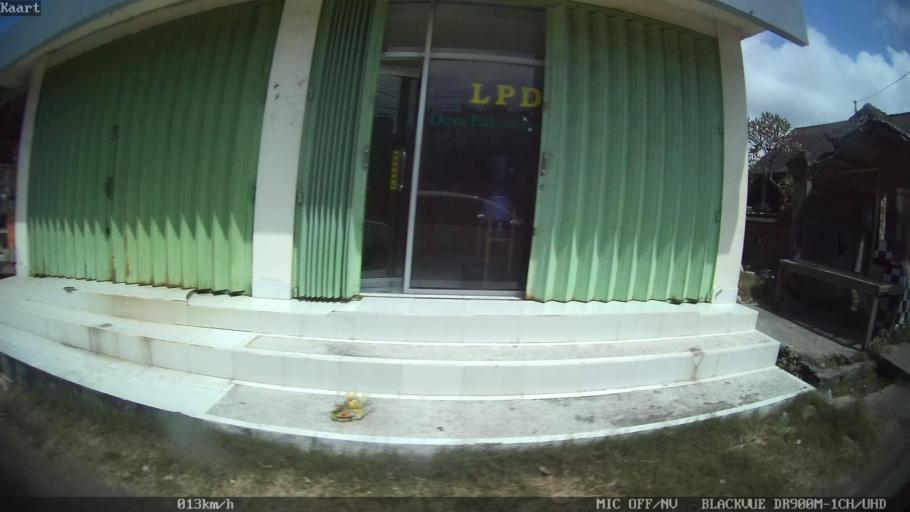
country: ID
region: Bali
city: Banjar Pasekan
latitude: -8.6027
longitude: 115.3094
